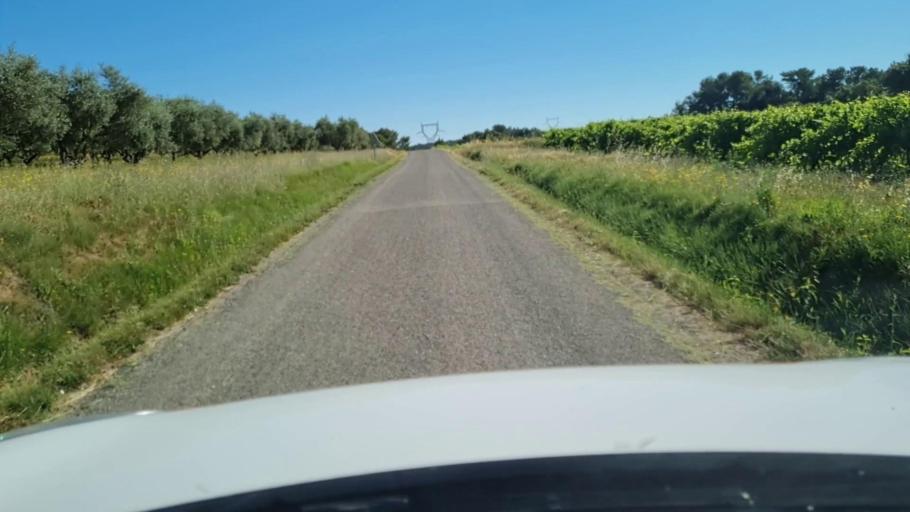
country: FR
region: Languedoc-Roussillon
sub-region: Departement du Gard
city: Sommieres
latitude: 43.8167
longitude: 4.0503
